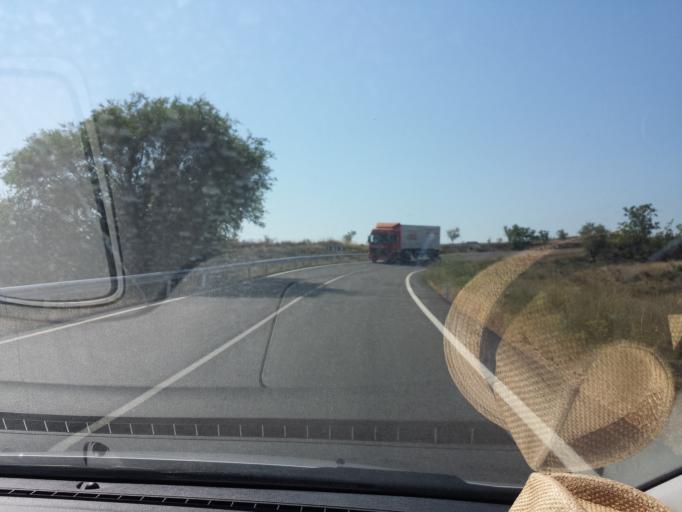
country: ES
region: Aragon
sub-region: Provincia de Zaragoza
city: Paracuellos de Jiloca
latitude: 41.3137
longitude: -1.6689
